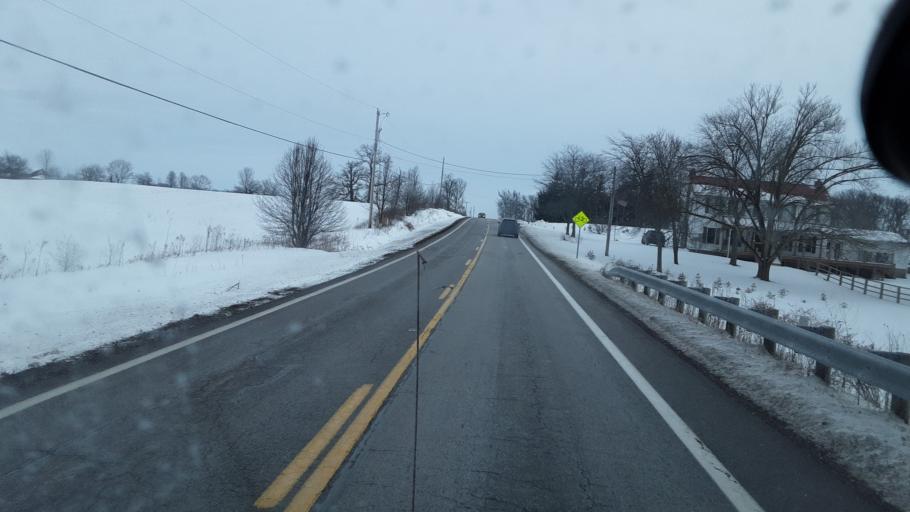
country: US
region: Ohio
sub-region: Union County
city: Marysville
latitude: 40.1849
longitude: -83.3450
